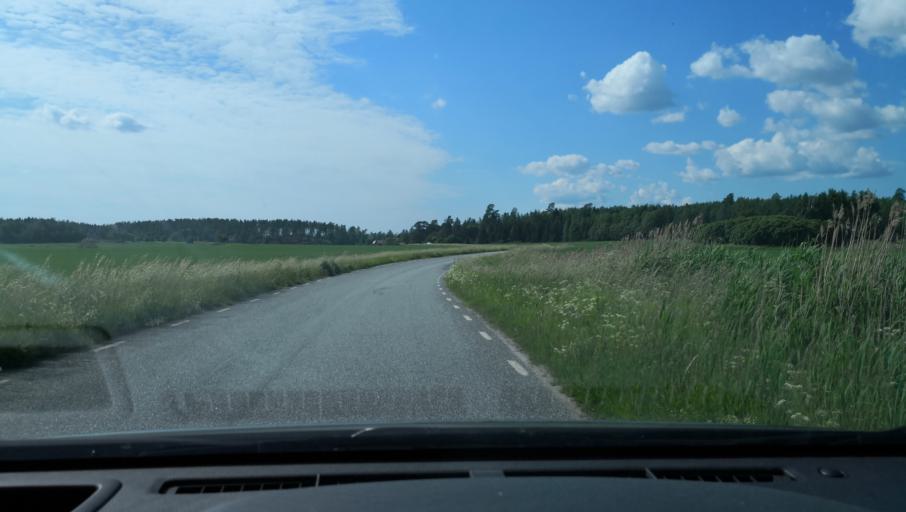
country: SE
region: Uppsala
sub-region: Enkopings Kommun
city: Orsundsbro
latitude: 59.8376
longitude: 17.2993
